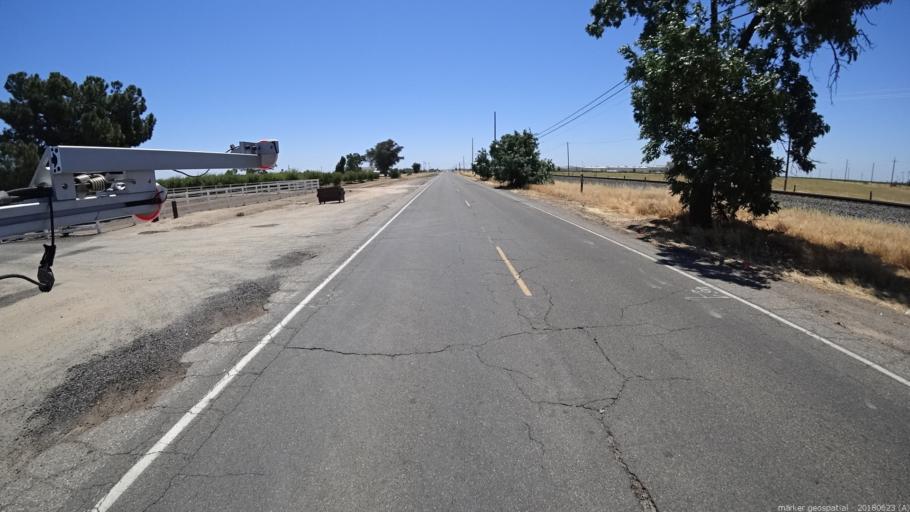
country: US
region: California
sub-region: Madera County
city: Chowchilla
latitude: 37.1015
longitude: -120.2283
